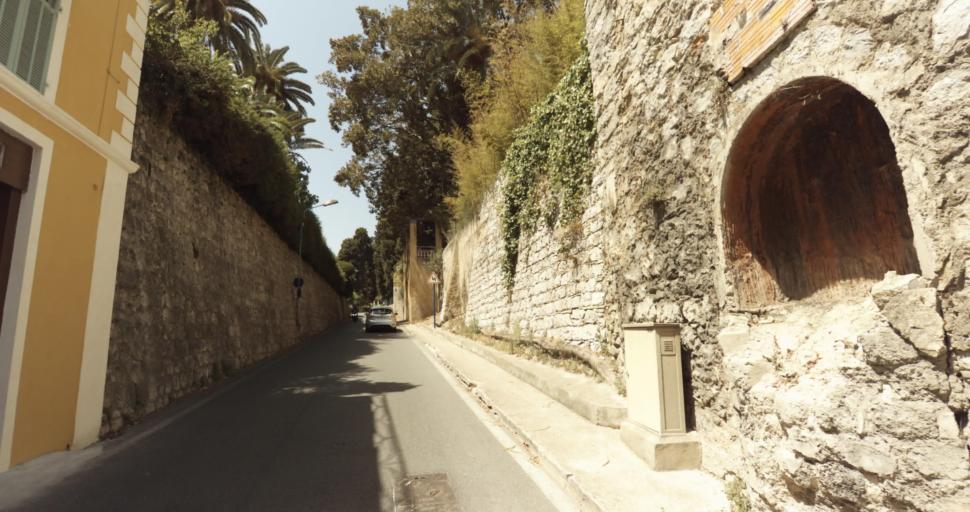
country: FR
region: Provence-Alpes-Cote d'Azur
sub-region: Departement des Alpes-Maritimes
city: Menton
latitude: 43.7851
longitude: 7.5160
